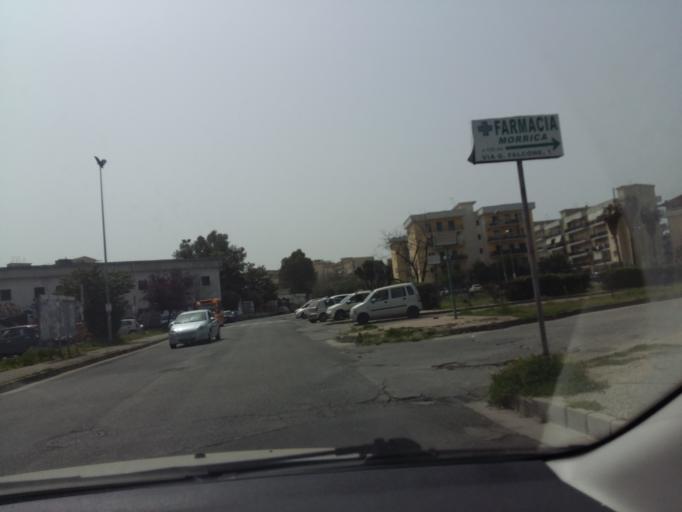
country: IT
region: Campania
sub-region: Provincia di Napoli
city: Mugnano di Napoli
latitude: 40.9005
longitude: 14.2012
